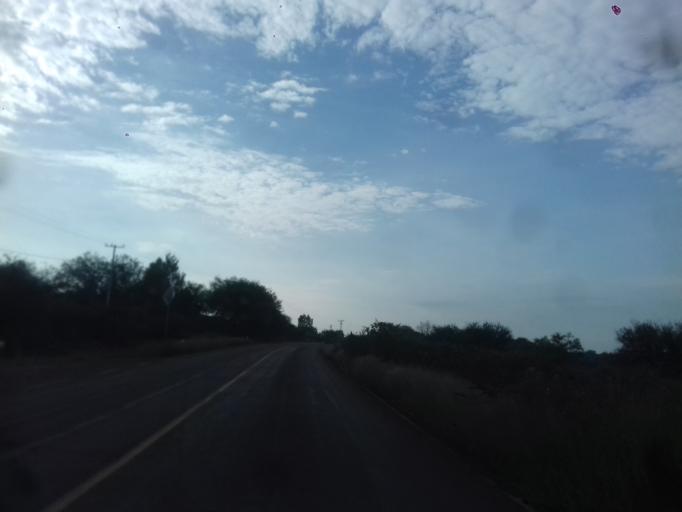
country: MX
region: Aguascalientes
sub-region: Aguascalientes
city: San Sebastian [Fraccionamiento]
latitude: 21.7966
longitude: -102.2412
